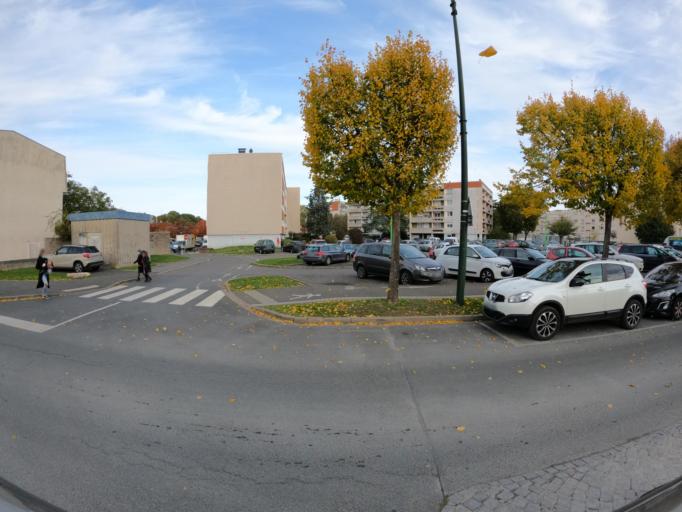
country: FR
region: Ile-de-France
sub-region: Departement de Seine-et-Marne
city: Pontault-Combault
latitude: 48.7985
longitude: 2.6074
